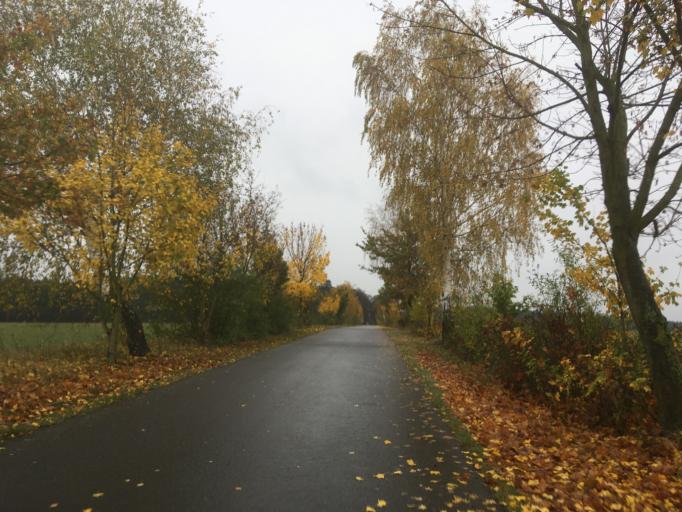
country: DE
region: Brandenburg
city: Neu Zauche
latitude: 52.0254
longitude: 14.1233
